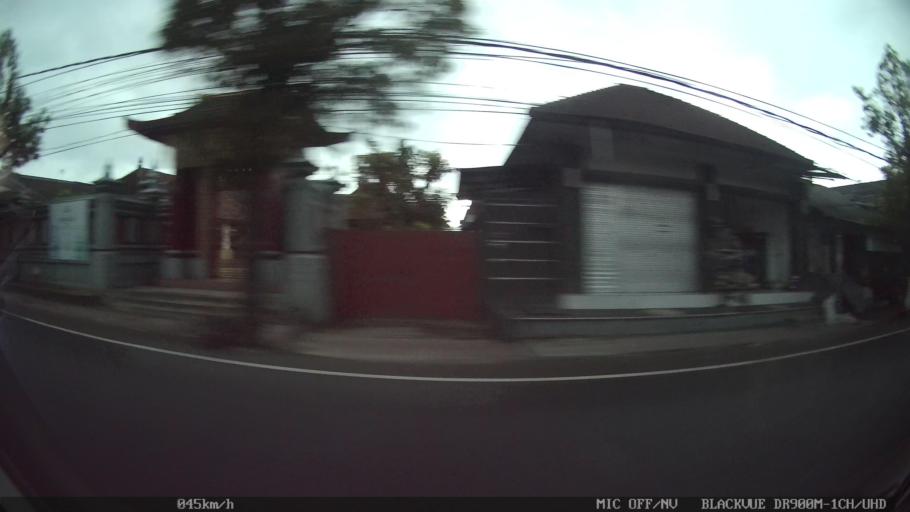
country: ID
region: Bali
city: Banjar Pasekan
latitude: -8.6004
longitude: 115.2830
